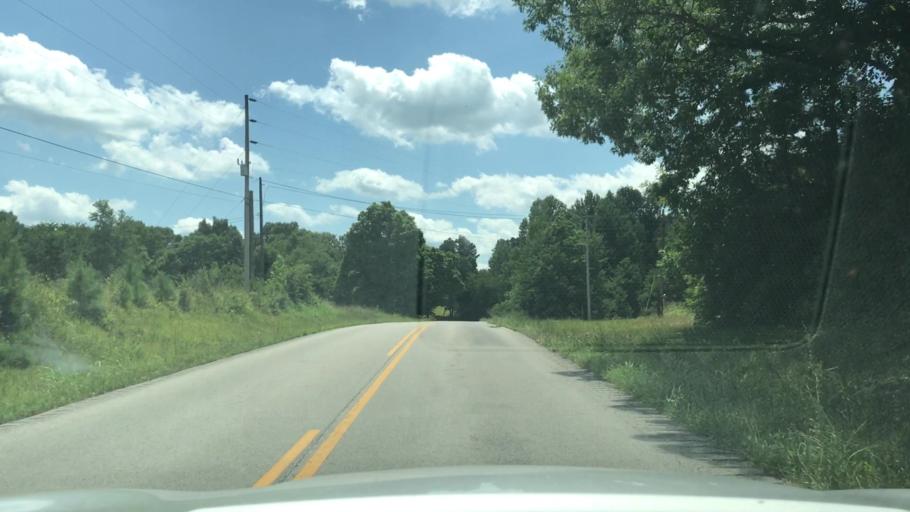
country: US
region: Kentucky
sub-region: Hopkins County
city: Nortonville
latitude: 37.1167
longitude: -87.3245
